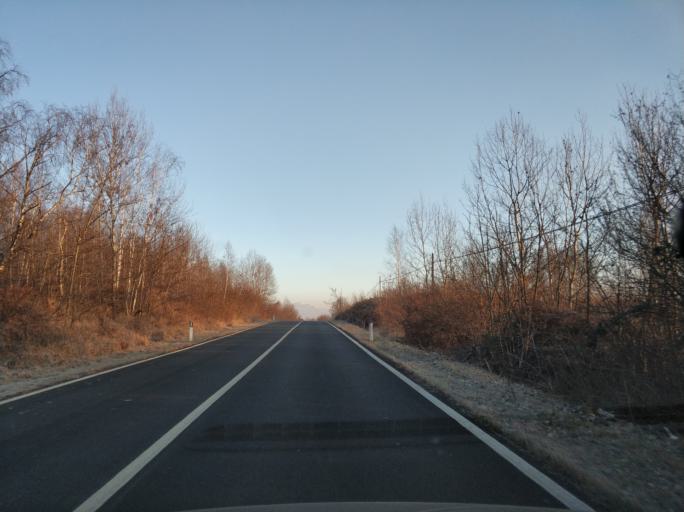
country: IT
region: Piedmont
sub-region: Provincia di Torino
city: Grosso
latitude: 45.2705
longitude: 7.5792
